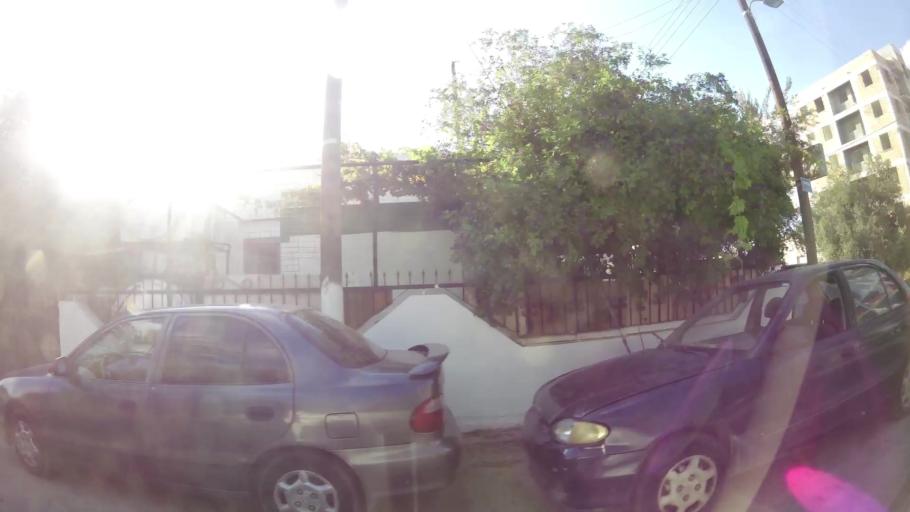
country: CY
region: Lefkosia
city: Nicosia
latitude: 35.1982
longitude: 33.3593
